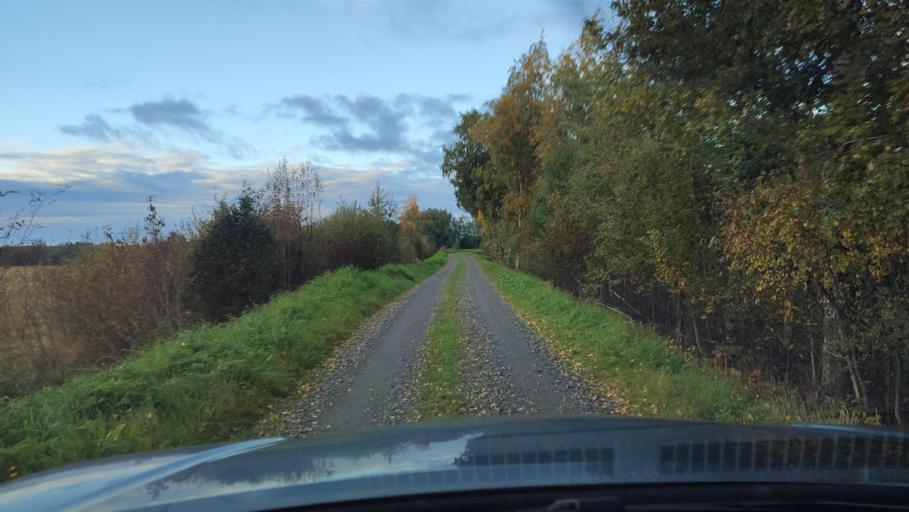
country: FI
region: Ostrobothnia
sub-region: Sydosterbotten
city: Kristinestad
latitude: 62.2330
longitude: 21.4508
